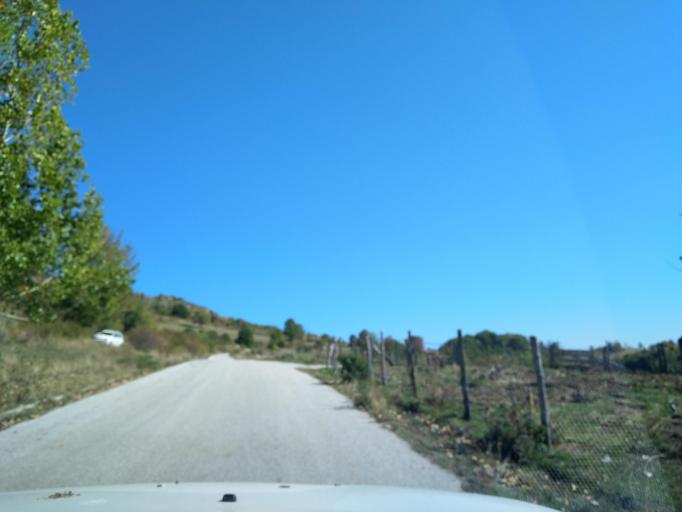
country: RS
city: Sokolovica
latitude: 43.2507
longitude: 20.3202
